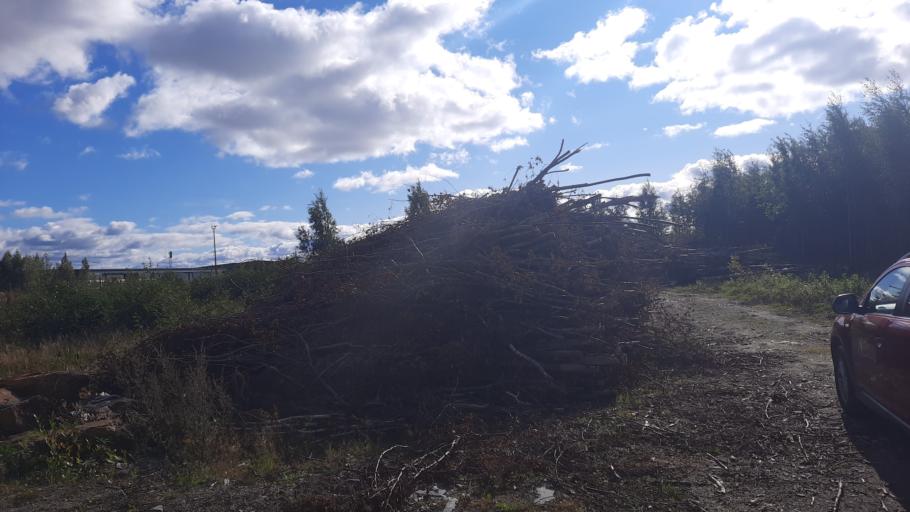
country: FI
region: North Karelia
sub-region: Joensuu
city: Joensuu
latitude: 62.5857
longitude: 29.7515
